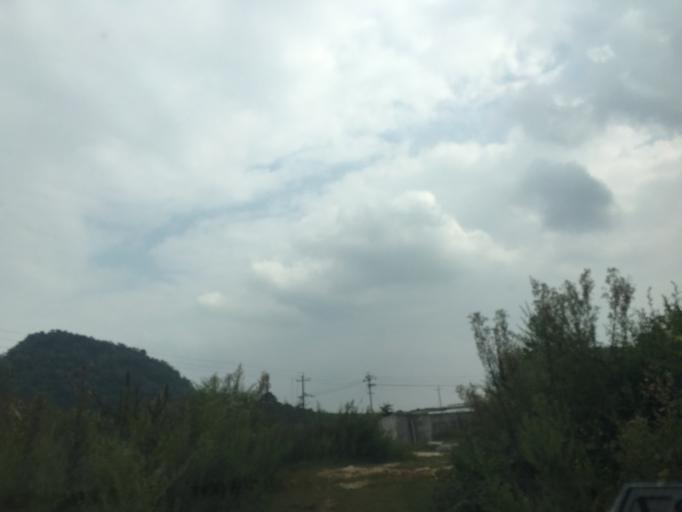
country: CN
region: Guangxi Zhuangzu Zizhiqu
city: Xinzhou
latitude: 25.4874
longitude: 105.6509
